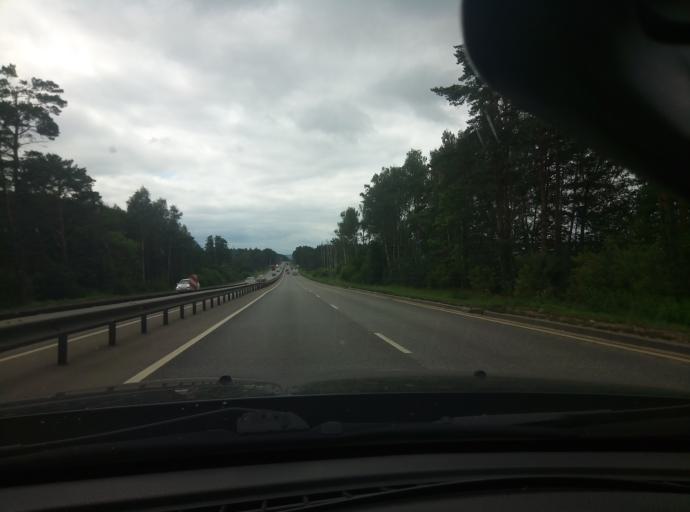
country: RU
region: Kaluga
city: Obninsk
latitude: 55.0719
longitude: 36.6259
